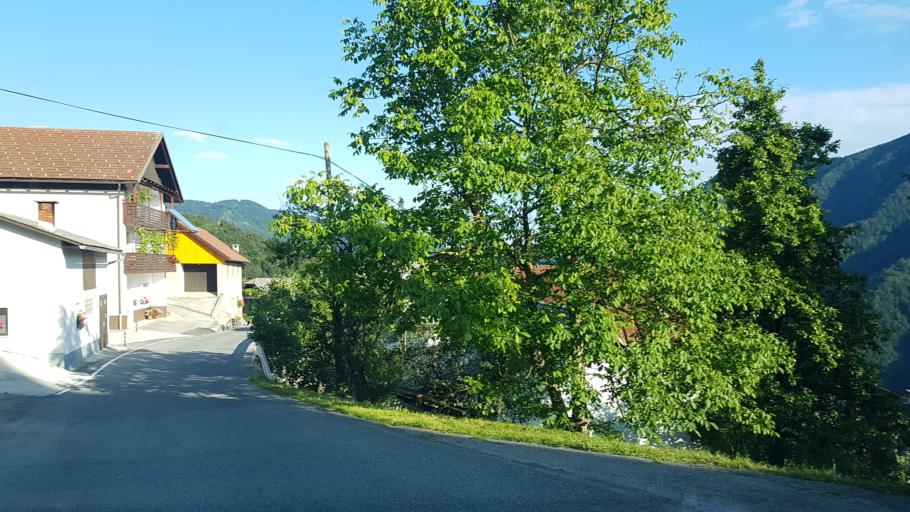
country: SI
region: Cerkno
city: Cerkno
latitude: 46.0793
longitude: 13.9918
